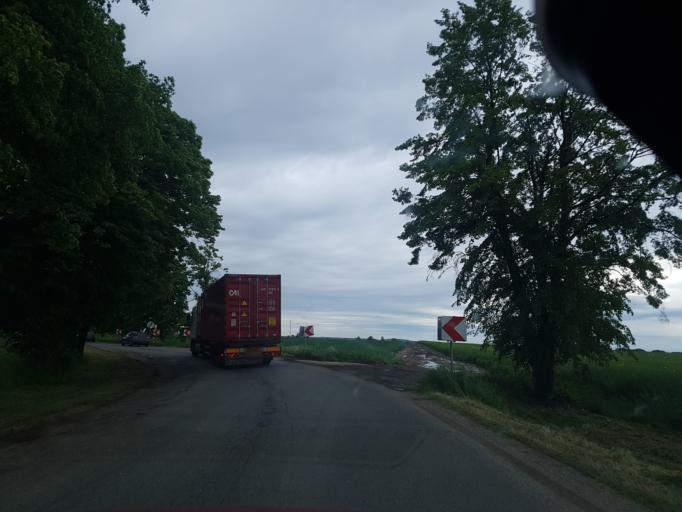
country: PL
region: Lower Silesian Voivodeship
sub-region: Powiat wroclawski
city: Kobierzyce
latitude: 50.9279
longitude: 16.9463
